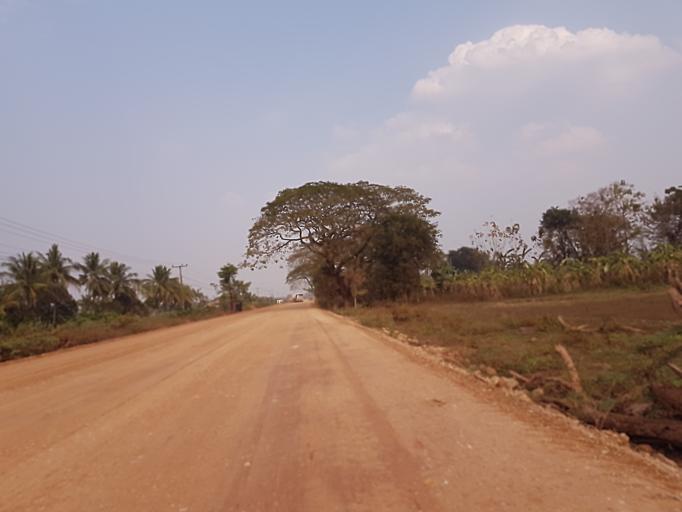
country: TH
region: Nong Khai
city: Nong Khai
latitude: 17.9798
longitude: 102.8760
